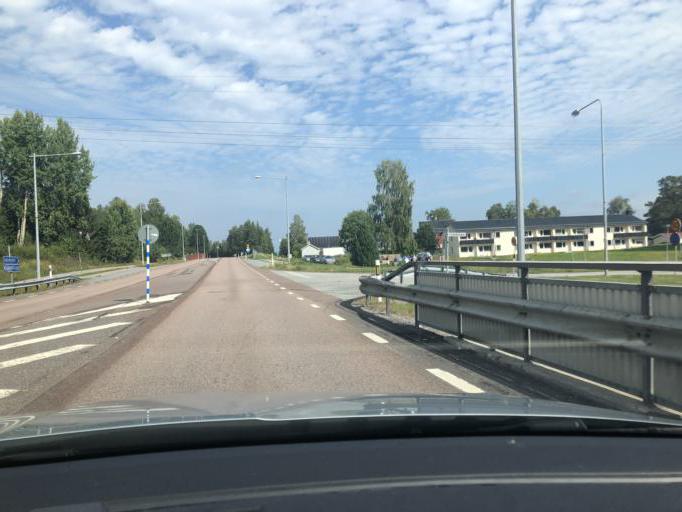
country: SE
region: Vaesternorrland
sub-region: Kramfors Kommun
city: Kramfors
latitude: 62.8071
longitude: 17.8670
